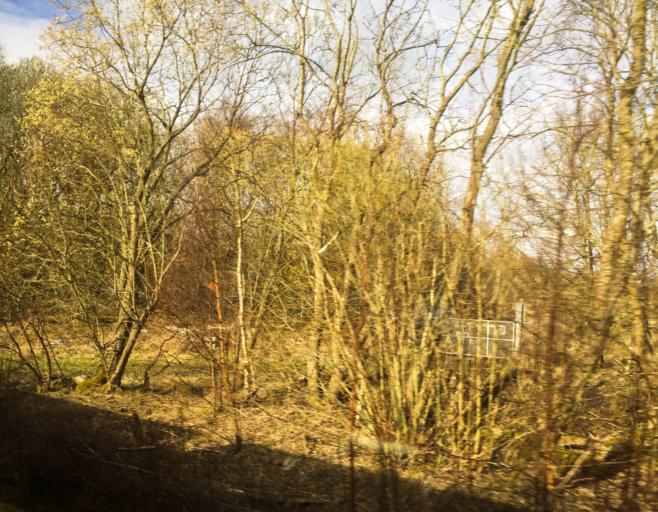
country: GB
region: Scotland
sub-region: North Lanarkshire
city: Glenboig
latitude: 55.8782
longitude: -4.0472
